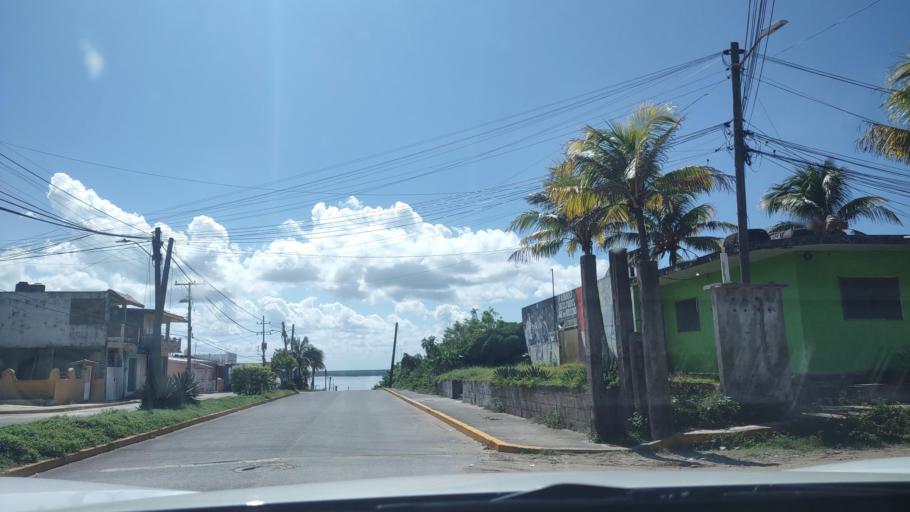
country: MX
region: Veracruz
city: Heroica Alvarado
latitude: 18.7809
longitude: -95.7709
